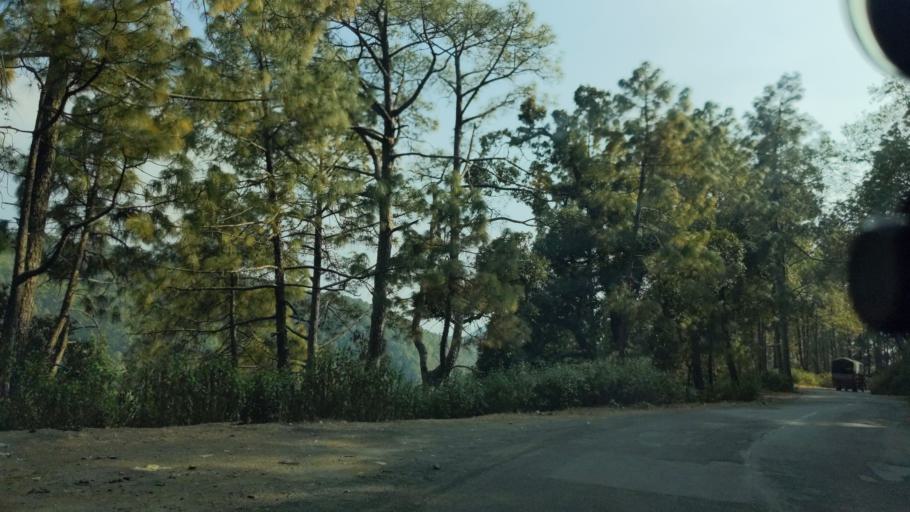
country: IN
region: Uttarakhand
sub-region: Naini Tal
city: Bhowali
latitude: 29.4012
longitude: 79.5381
